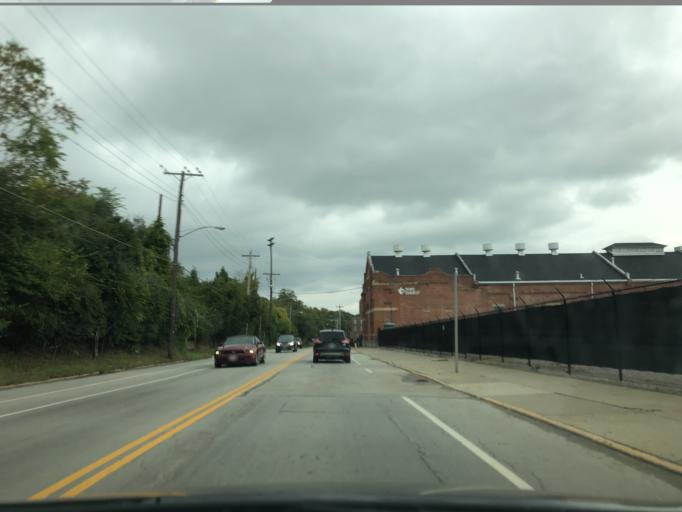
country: US
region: Kentucky
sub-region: Campbell County
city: Dayton
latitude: 39.1223
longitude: -84.4537
